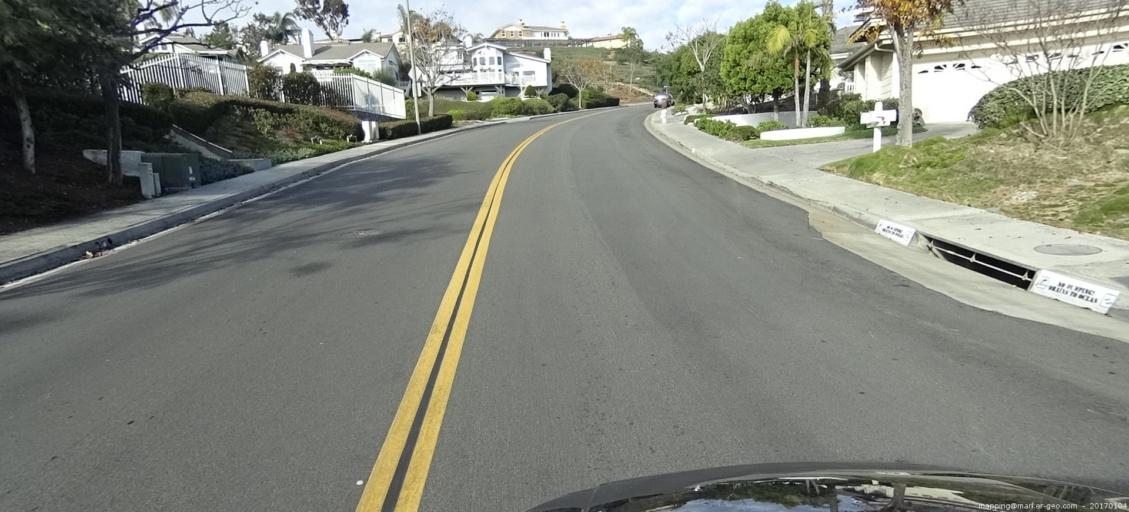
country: US
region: California
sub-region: Orange County
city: Dana Point
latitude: 33.4678
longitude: -117.6877
